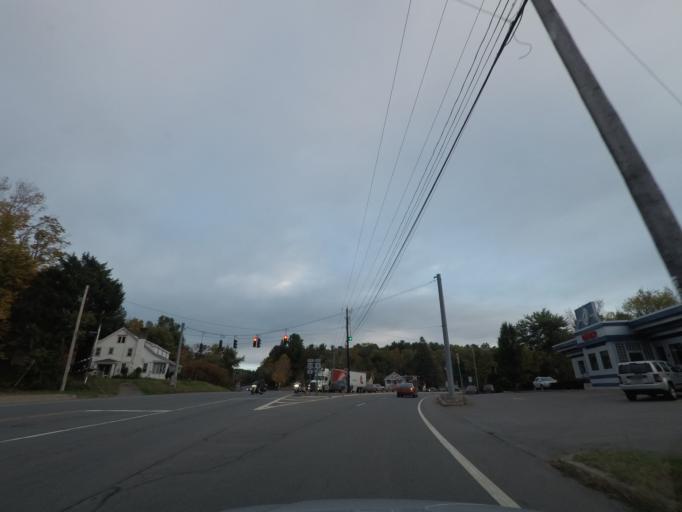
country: US
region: New York
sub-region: Rensselaer County
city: East Greenbush
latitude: 42.5488
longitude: -73.6716
